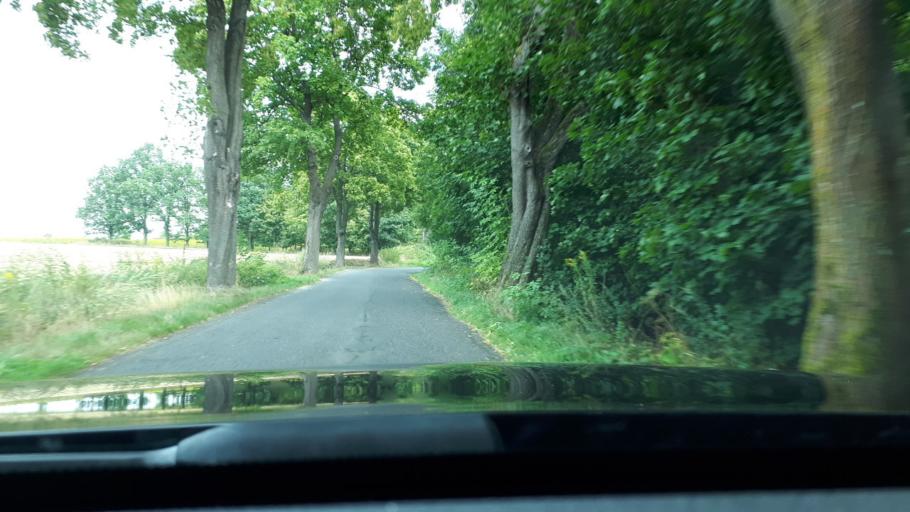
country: PL
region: Lower Silesian Voivodeship
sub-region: Powiat zlotoryjski
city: Olszanica
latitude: 51.2302
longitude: 15.7976
